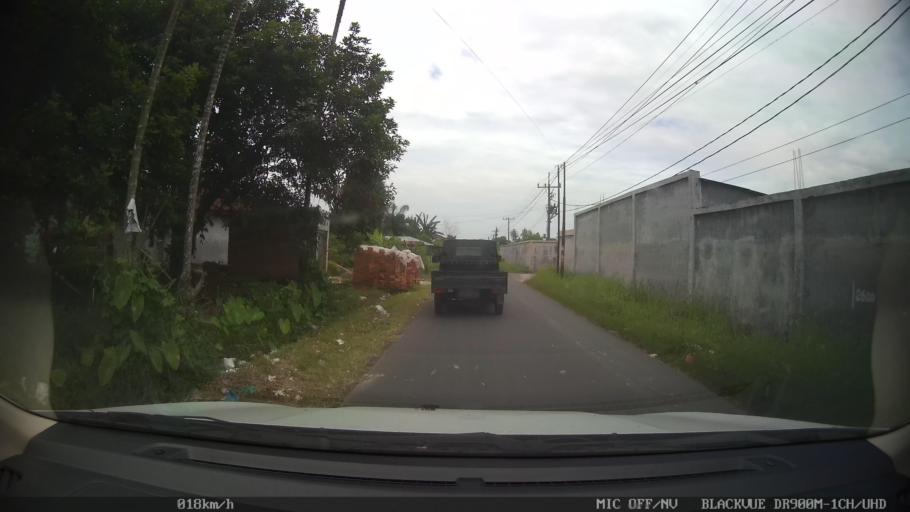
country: ID
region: North Sumatra
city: Binjai
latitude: 3.6207
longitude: 98.5546
